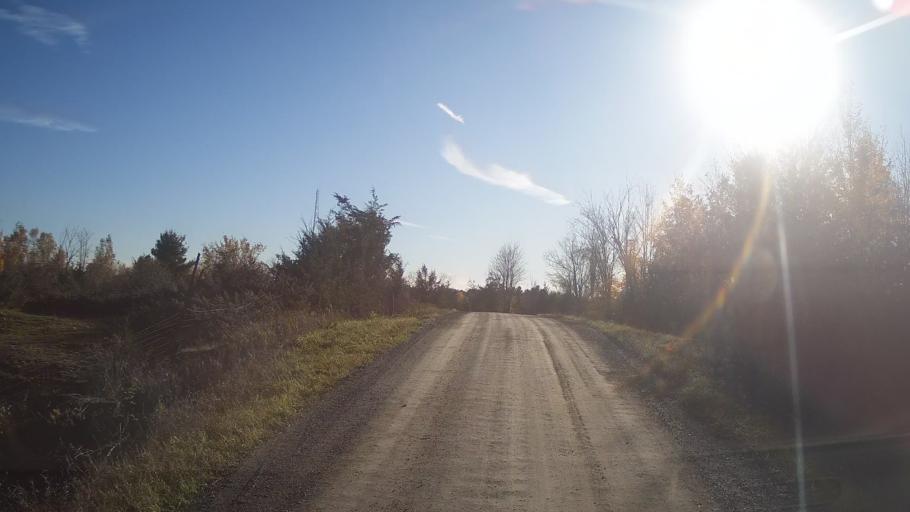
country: CA
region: Ontario
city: Perth
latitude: 44.7068
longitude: -76.4269
